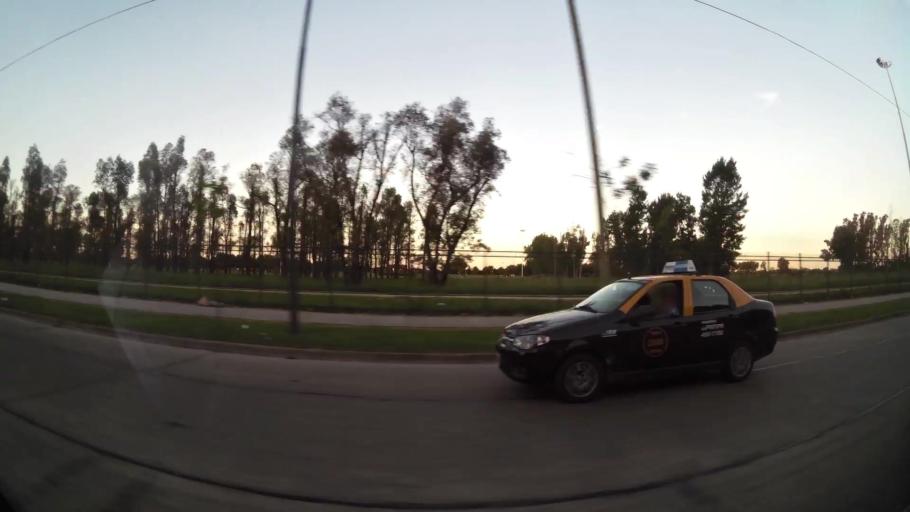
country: AR
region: Buenos Aires F.D.
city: Villa Lugano
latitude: -34.6672
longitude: -58.4666
